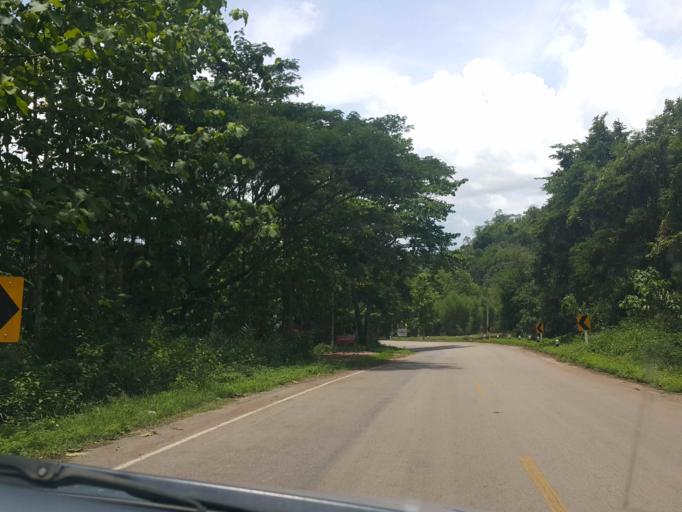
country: TH
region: Phayao
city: Chiang Muan
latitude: 18.8976
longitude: 100.1353
